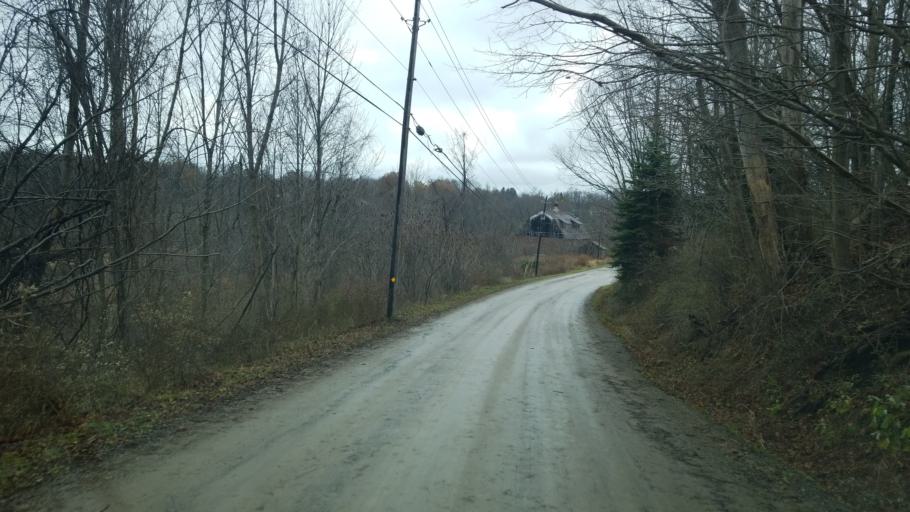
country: US
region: Ohio
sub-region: Ashtabula County
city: Conneaut
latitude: 41.9212
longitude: -80.6055
